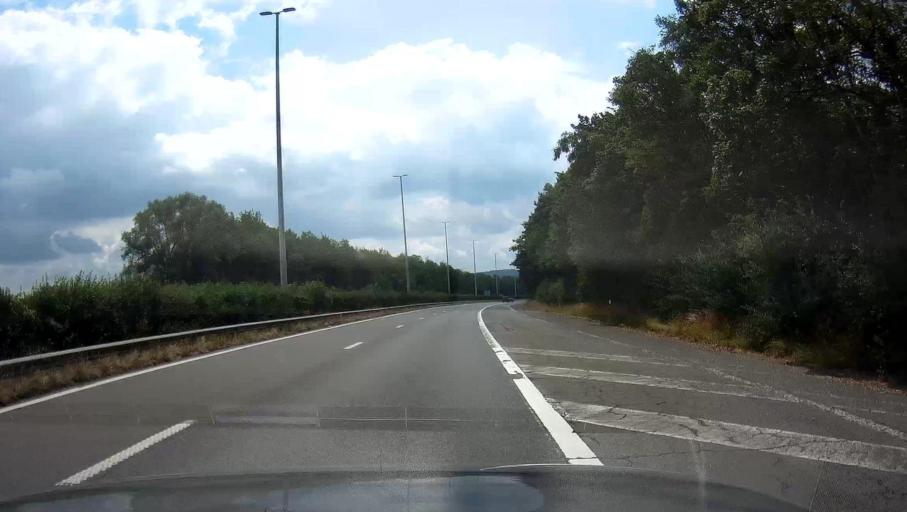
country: BE
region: Wallonia
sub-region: Province du Luxembourg
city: Aubange
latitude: 49.5709
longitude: 5.8215
